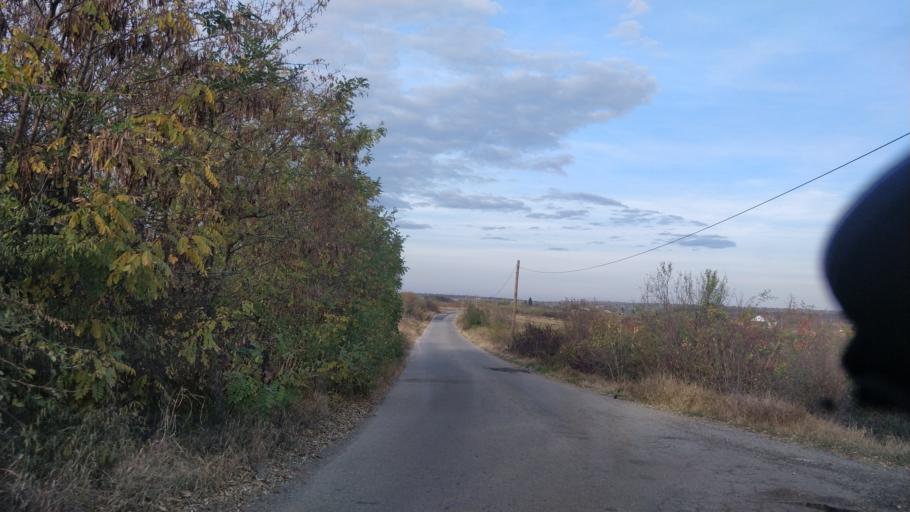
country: RO
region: Giurgiu
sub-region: Comuna Bucsani
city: Bucsani
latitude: 44.3544
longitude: 25.6577
